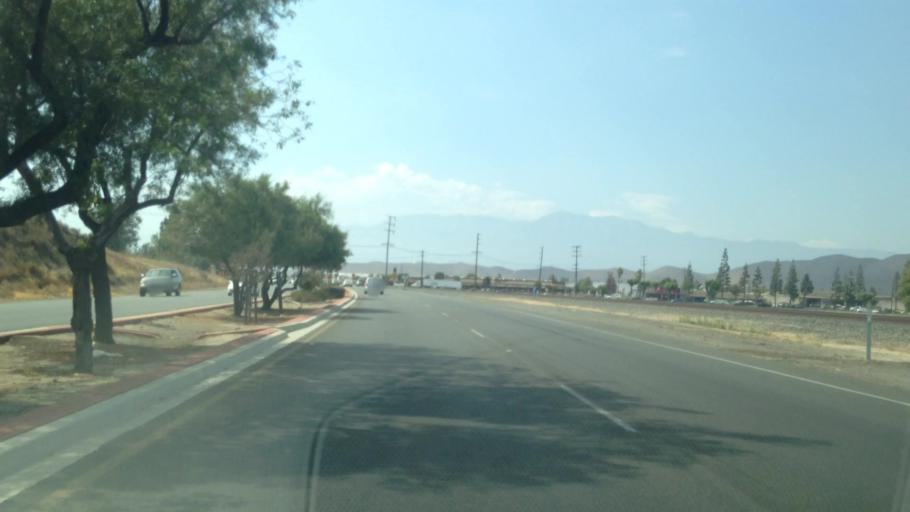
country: US
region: California
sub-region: Riverside County
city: Glen Avon
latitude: 33.9940
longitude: -117.4827
